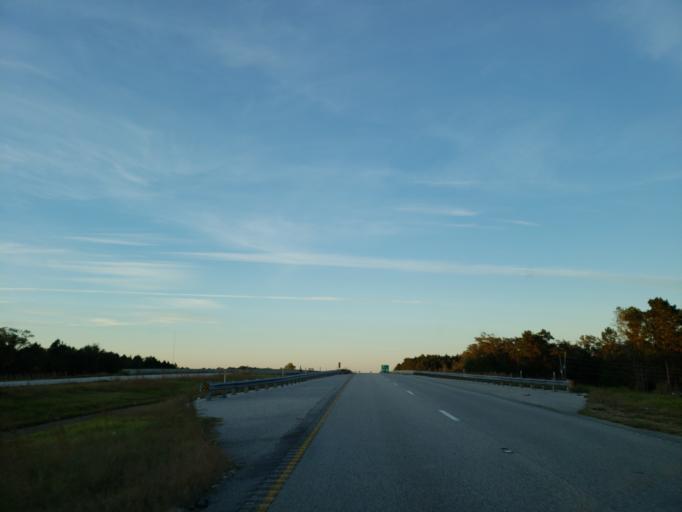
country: US
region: Mississippi
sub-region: Wayne County
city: Belmont
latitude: 31.4443
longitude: -88.4653
